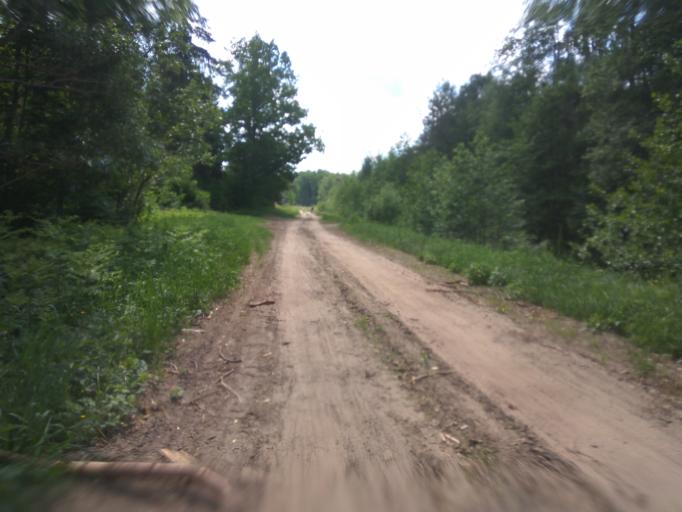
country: LV
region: Kuldigas Rajons
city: Kuldiga
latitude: 56.8848
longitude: 21.9729
